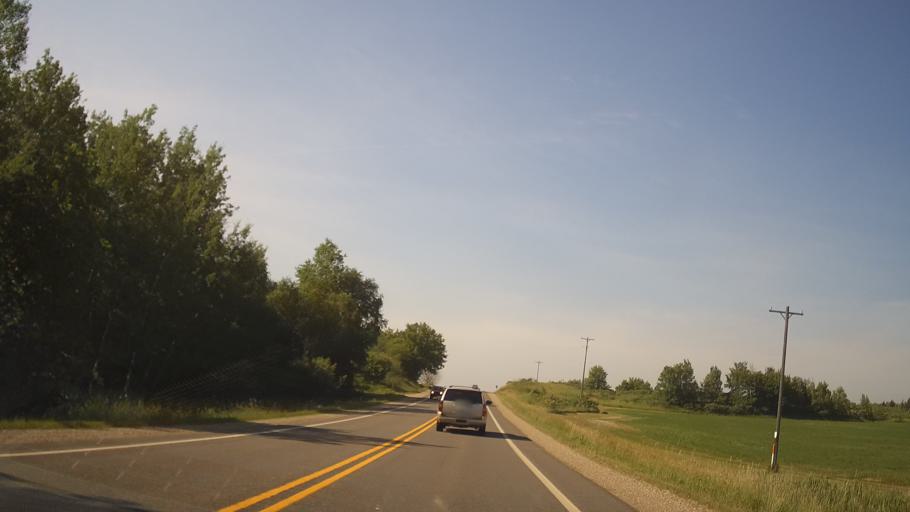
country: US
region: Michigan
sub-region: Ogemaw County
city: West Branch
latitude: 44.3403
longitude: -84.1258
